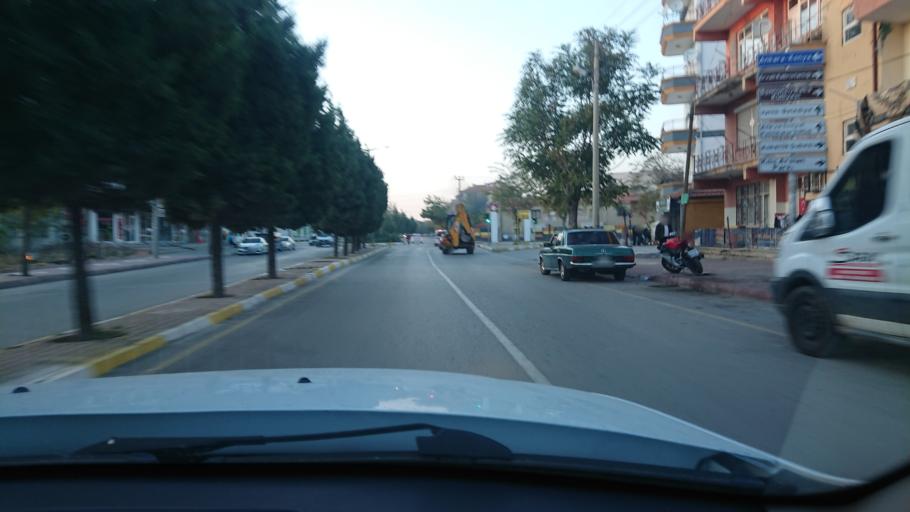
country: TR
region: Aksaray
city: Aksaray
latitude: 38.3631
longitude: 34.0357
